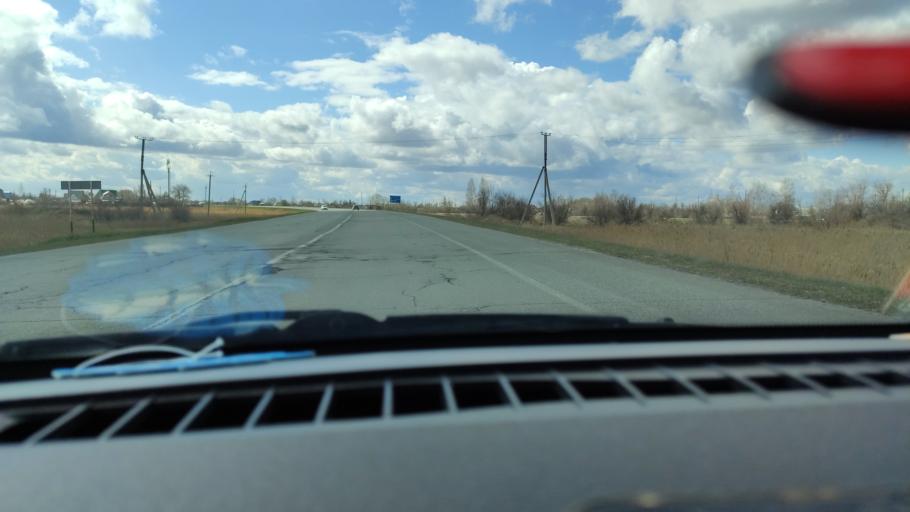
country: RU
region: Samara
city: Tol'yatti
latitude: 53.7138
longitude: 49.4241
